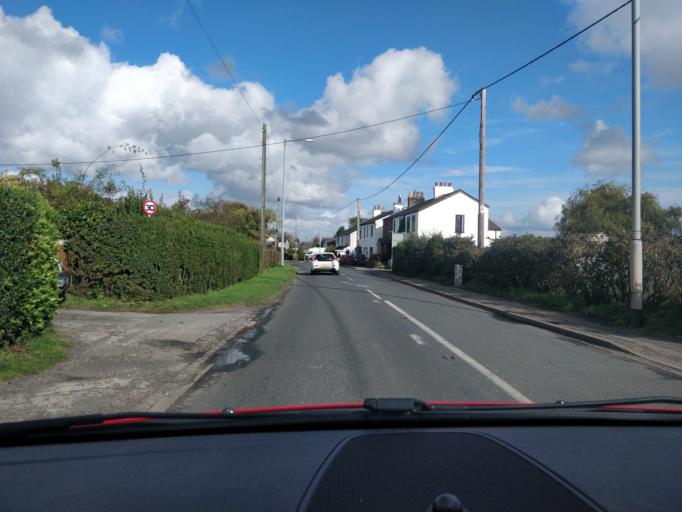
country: GB
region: England
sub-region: Lancashire
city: Parbold
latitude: 53.5980
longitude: -2.8039
